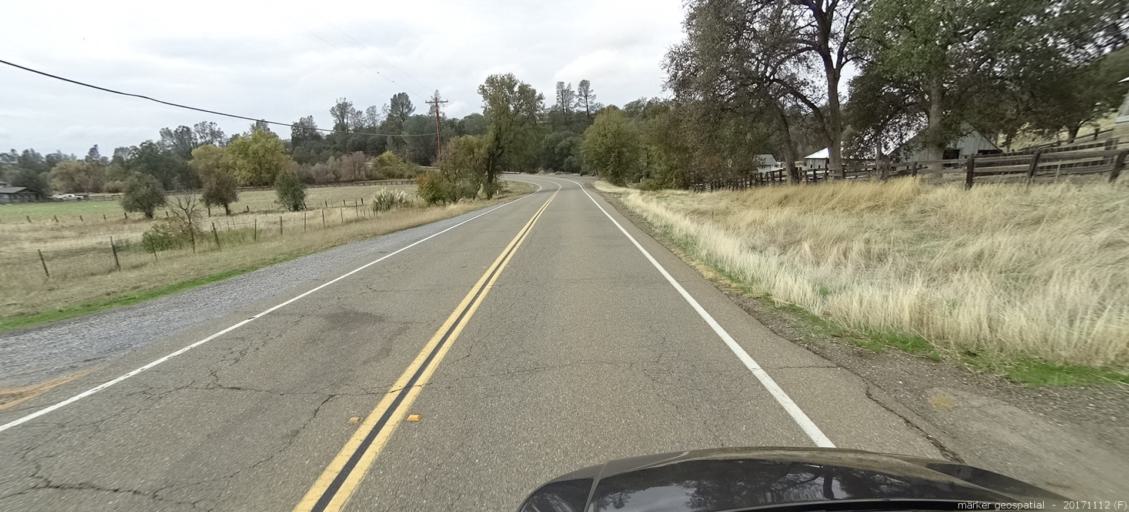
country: US
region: California
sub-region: Shasta County
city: Palo Cedro
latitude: 40.4858
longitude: -122.1497
